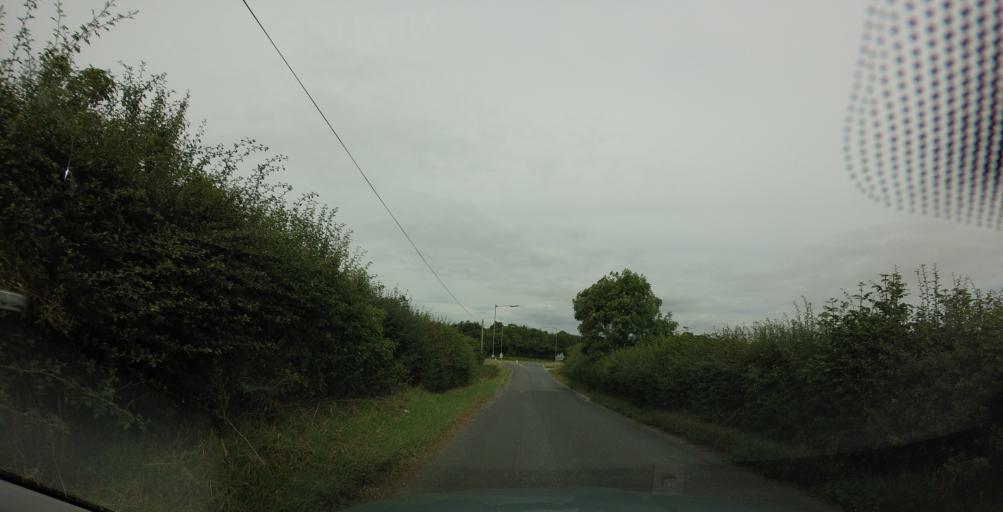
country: GB
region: England
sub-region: North Yorkshire
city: Ripon
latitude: 54.1225
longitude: -1.5180
